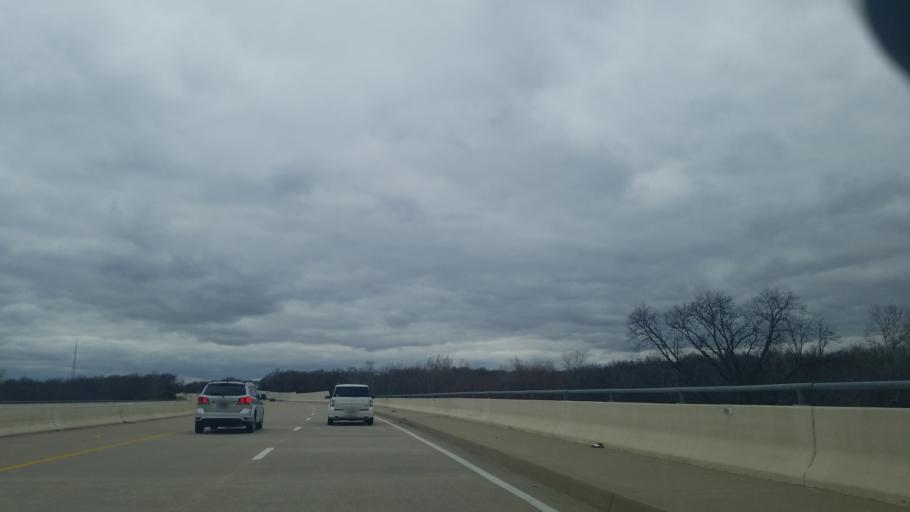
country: US
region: Texas
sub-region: Denton County
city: Copper Canyon
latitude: 33.1226
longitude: -97.0827
